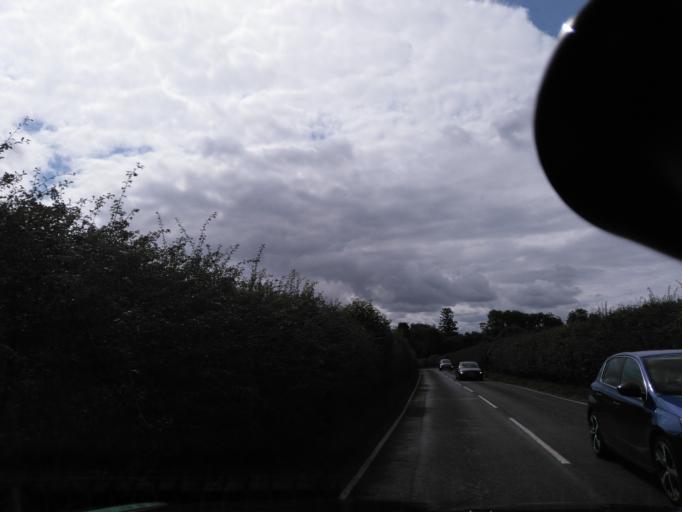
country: GB
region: England
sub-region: Dorset
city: Blandford Forum
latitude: 50.9281
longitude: -2.1641
